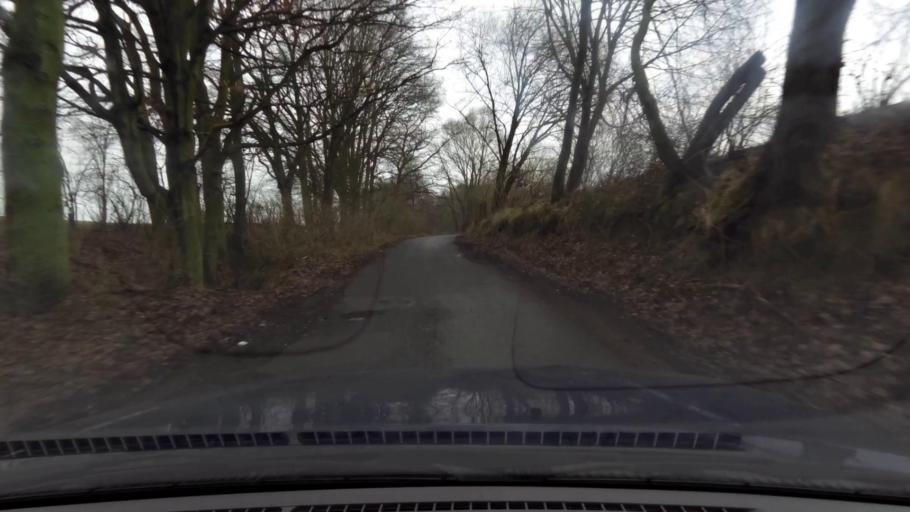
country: PL
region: West Pomeranian Voivodeship
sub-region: Powiat stargardzki
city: Stargard Szczecinski
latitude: 53.3323
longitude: 15.1303
